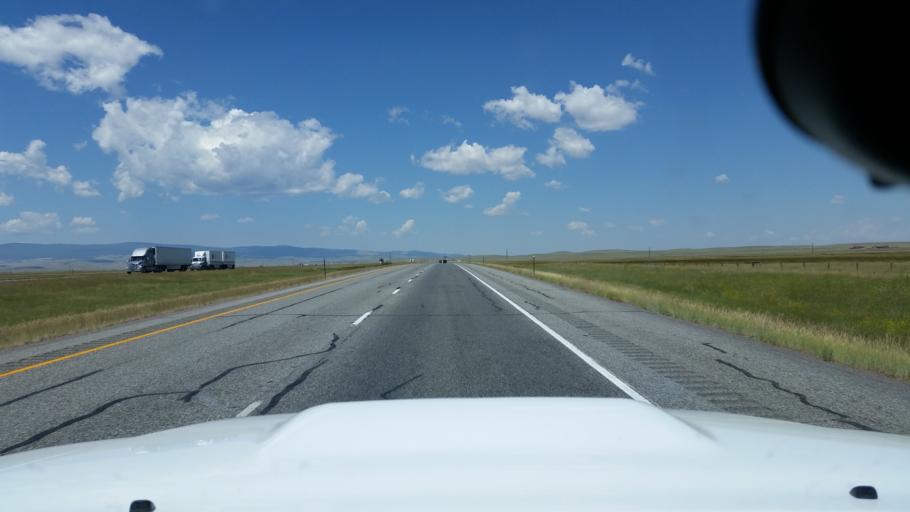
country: US
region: Wyoming
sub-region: Albany County
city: Laramie
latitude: 41.4152
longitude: -105.8487
